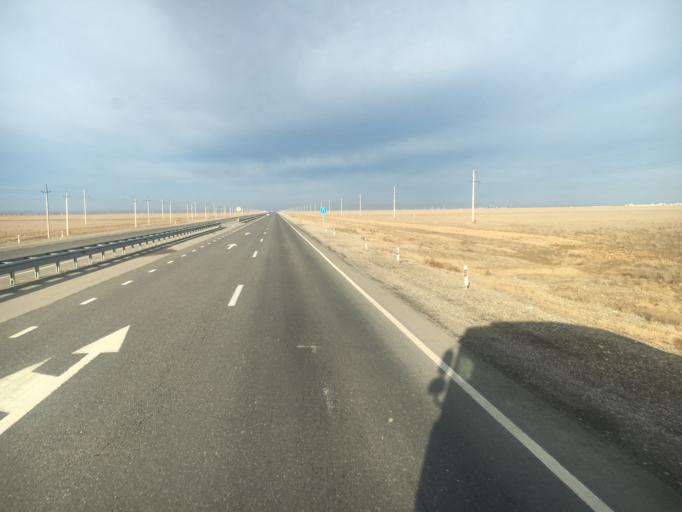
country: KZ
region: Ongtustik Qazaqstan
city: Turkestan
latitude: 43.4292
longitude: 67.9943
